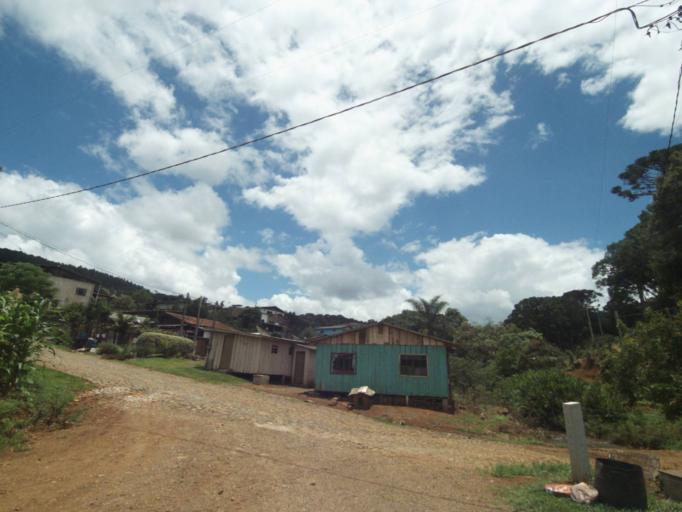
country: BR
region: Parana
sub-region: Pinhao
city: Pinhao
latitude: -26.1561
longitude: -51.5601
